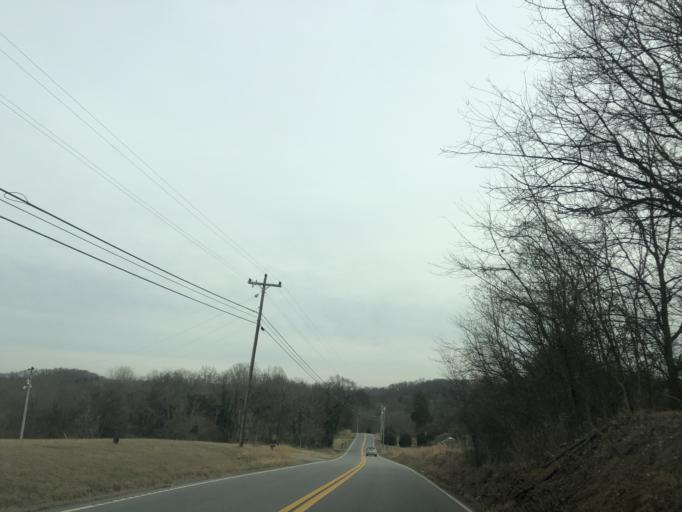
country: US
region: Tennessee
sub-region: Sumner County
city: White House
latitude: 36.4701
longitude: -86.5676
